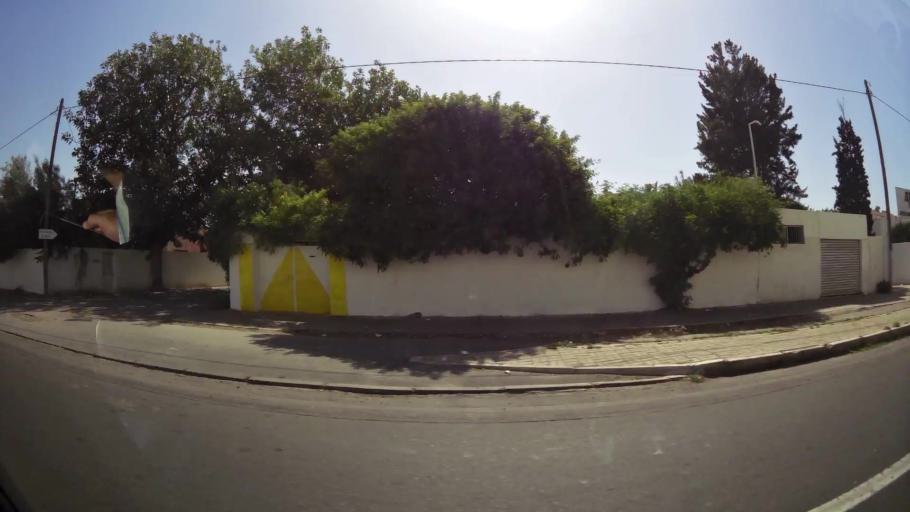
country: MA
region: Souss-Massa-Draa
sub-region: Inezgane-Ait Mellou
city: Inezgane
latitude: 30.3694
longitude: -9.5486
